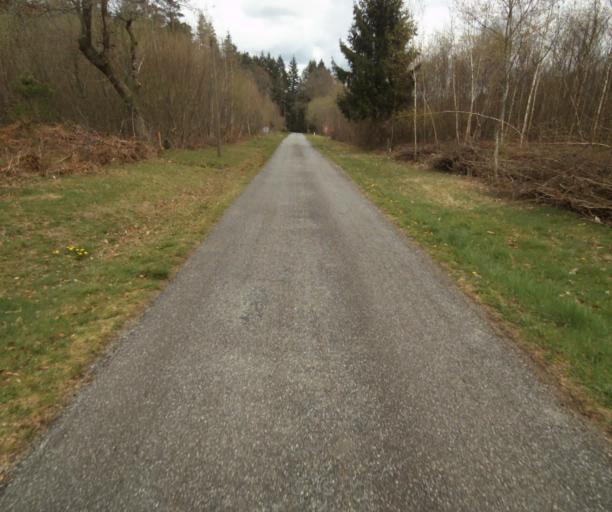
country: FR
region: Limousin
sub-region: Departement de la Correze
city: Correze
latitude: 45.3269
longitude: 1.9033
